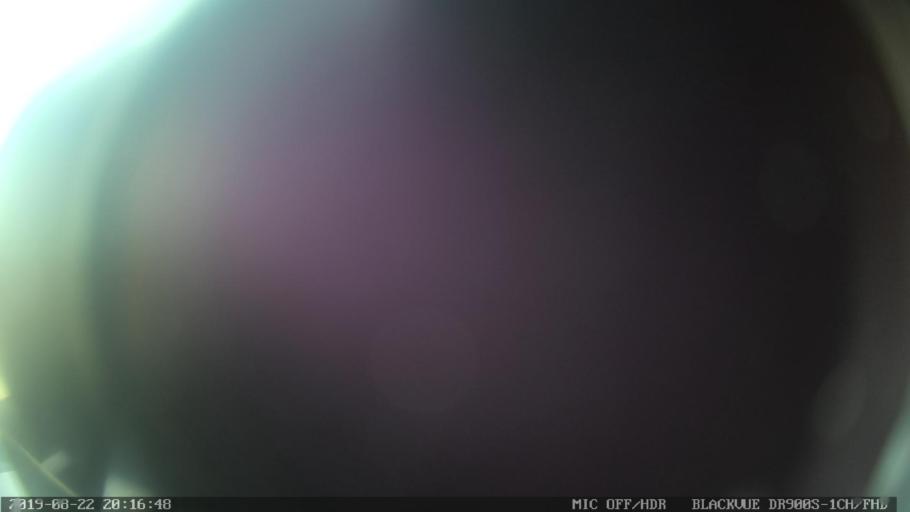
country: PT
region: Guarda
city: Alcains
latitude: 39.9242
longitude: -7.4593
